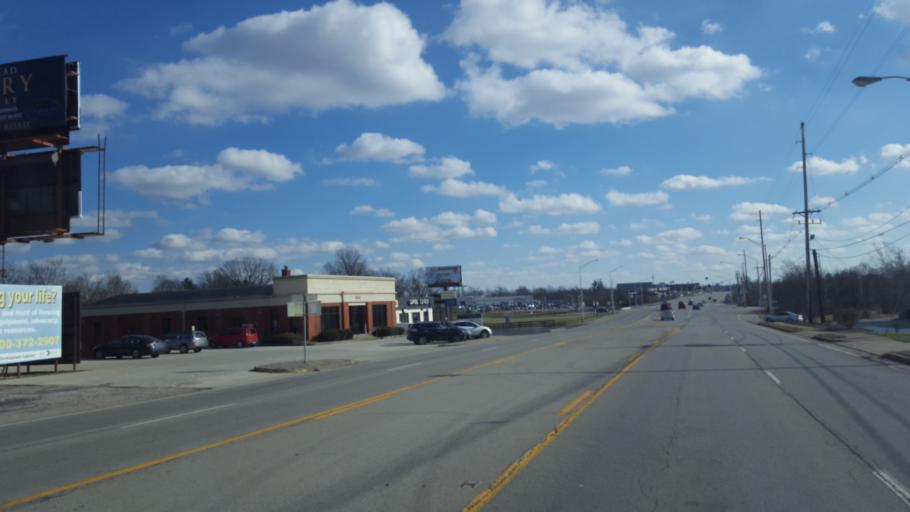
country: US
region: Kentucky
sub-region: Franklin County
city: Frankfort
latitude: 38.1907
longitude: -84.8235
